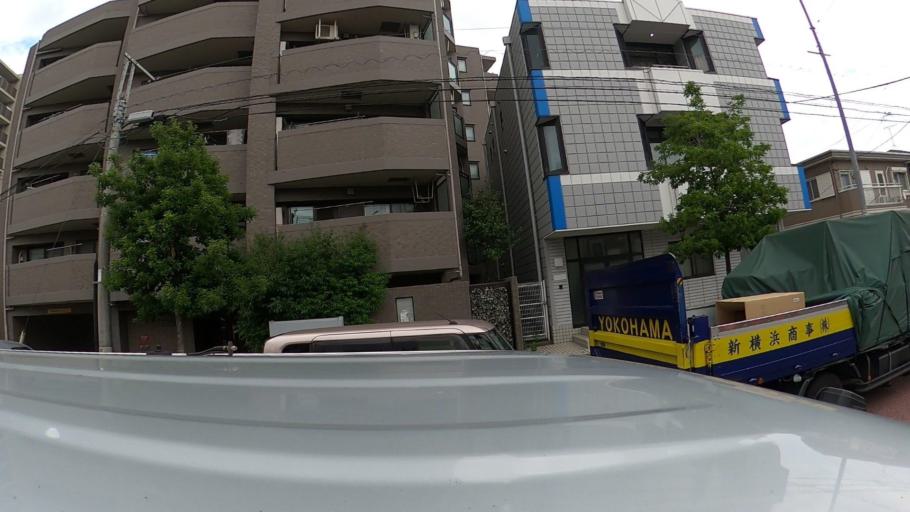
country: JP
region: Kanagawa
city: Yokohama
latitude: 35.4944
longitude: 139.6695
